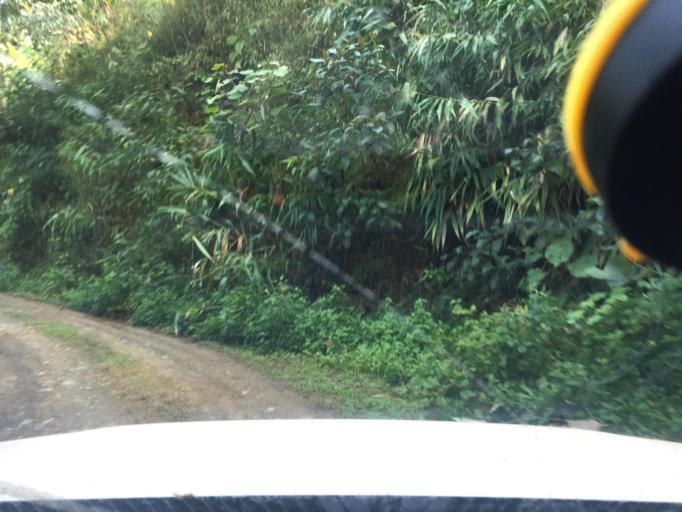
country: LA
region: Phongsali
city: Phongsali
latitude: 21.7035
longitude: 102.3978
